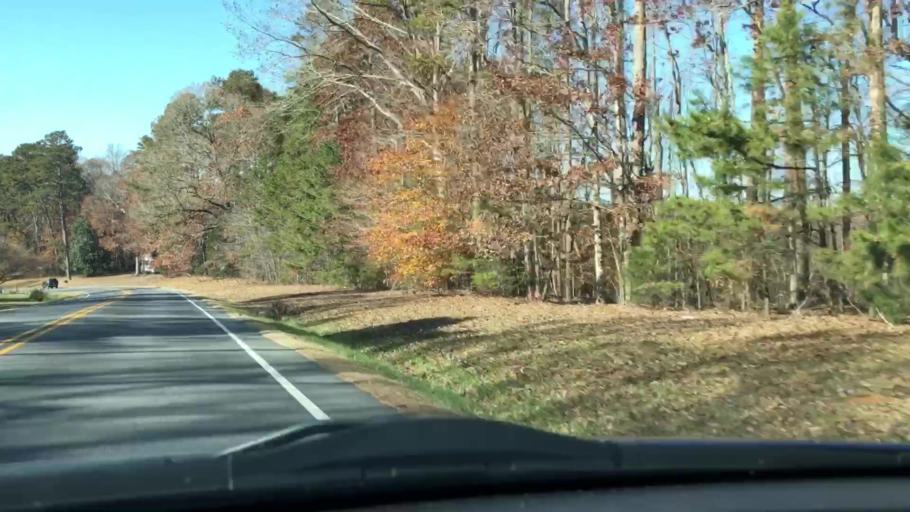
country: US
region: North Carolina
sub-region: Randolph County
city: Asheboro
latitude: 35.6741
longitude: -79.9355
